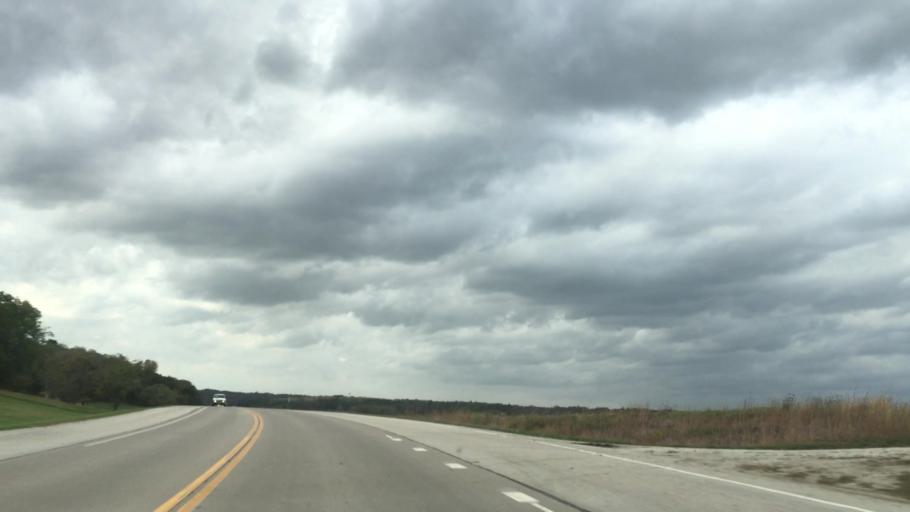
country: US
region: Minnesota
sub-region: Fillmore County
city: Preston
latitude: 43.7022
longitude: -92.1041
